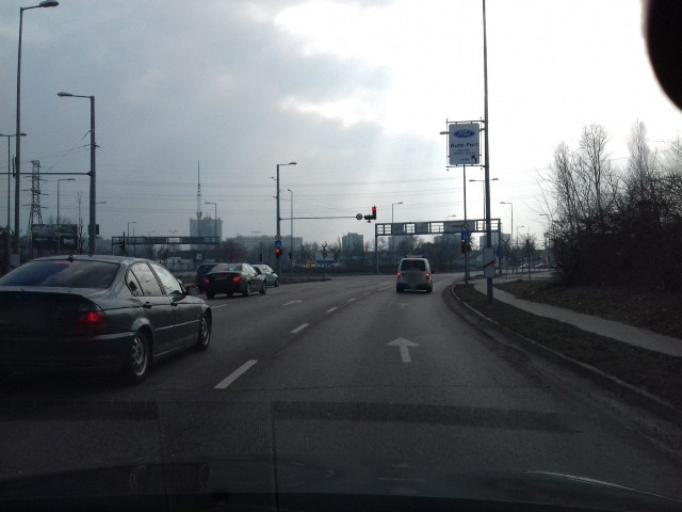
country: HU
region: Budapest
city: Budapest XXI. keruelet
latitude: 47.4408
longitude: 19.0720
